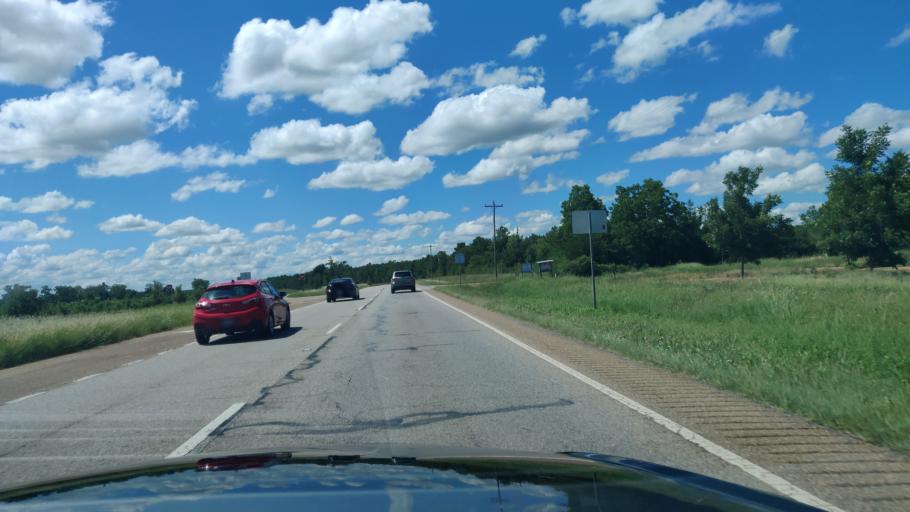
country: US
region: Georgia
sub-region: Webster County
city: Preston
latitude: 31.9423
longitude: -84.5703
